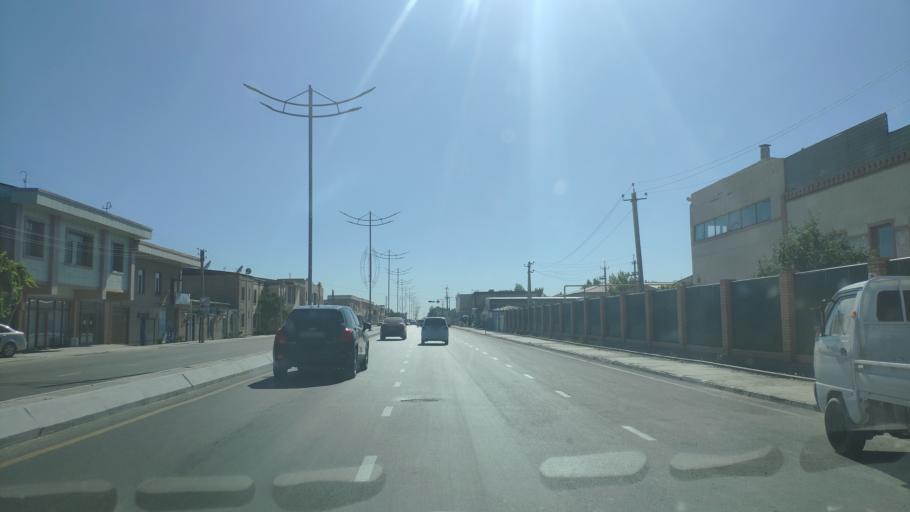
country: UZ
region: Bukhara
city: Bukhara
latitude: 39.7728
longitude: 64.3904
